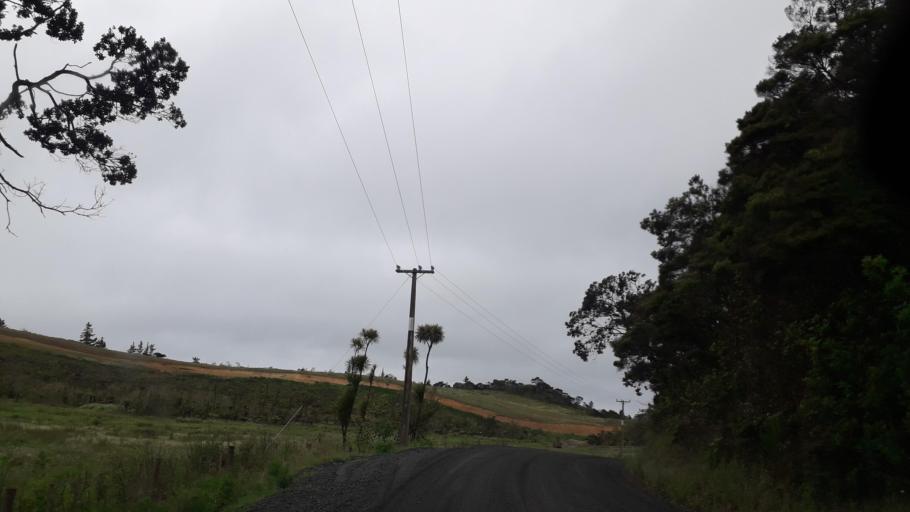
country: NZ
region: Northland
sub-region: Far North District
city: Paihia
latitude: -35.2399
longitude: 174.2482
